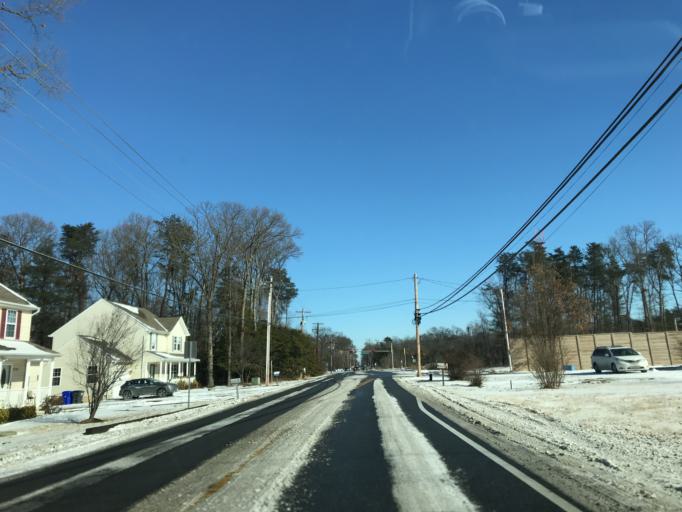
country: US
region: Maryland
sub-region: Charles County
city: Saint Charles
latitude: 38.6083
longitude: -76.9250
